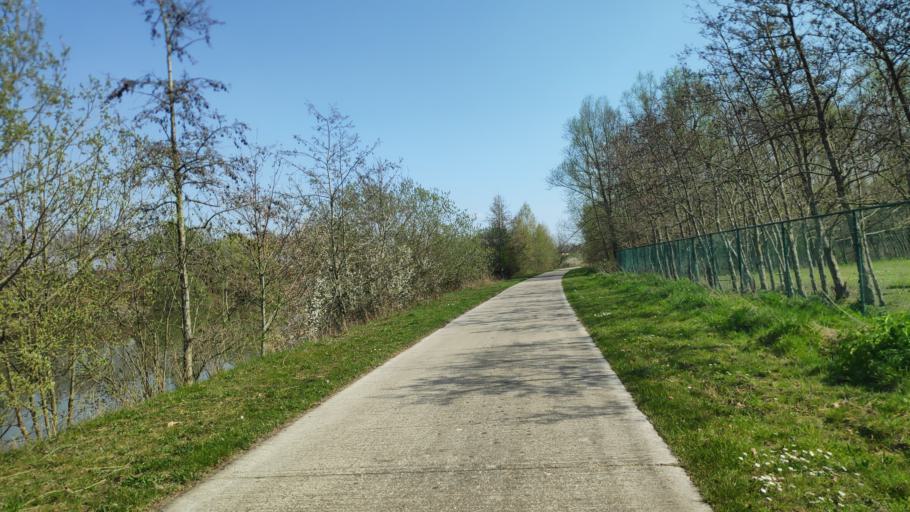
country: BE
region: Flanders
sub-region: Provincie West-Vlaanderen
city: Beernem
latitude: 51.1308
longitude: 3.3655
